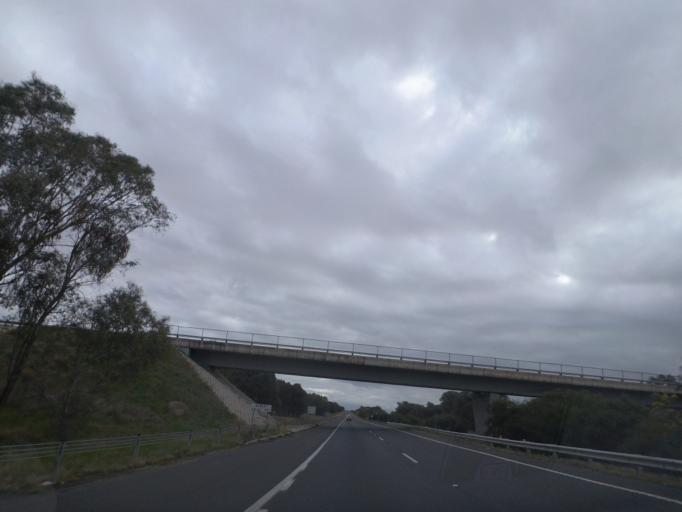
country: AU
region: New South Wales
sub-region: Corowa Shire
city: Howlong
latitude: -36.0831
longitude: 146.7289
